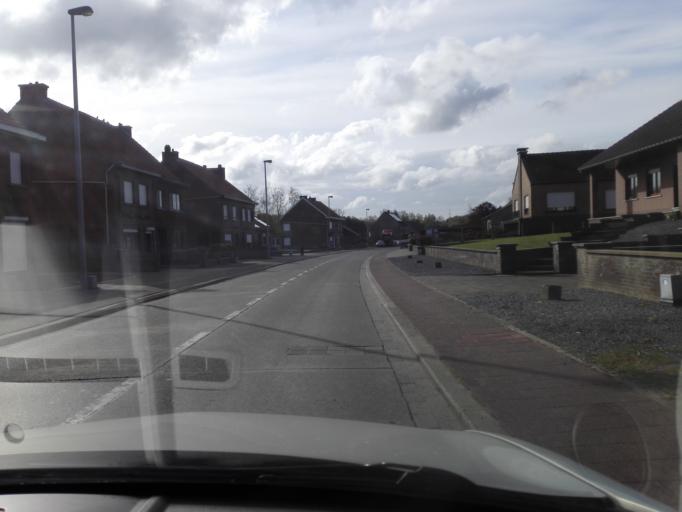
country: BE
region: Flanders
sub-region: Provincie Vlaams-Brabant
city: Aarschot
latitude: 50.9650
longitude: 4.8986
